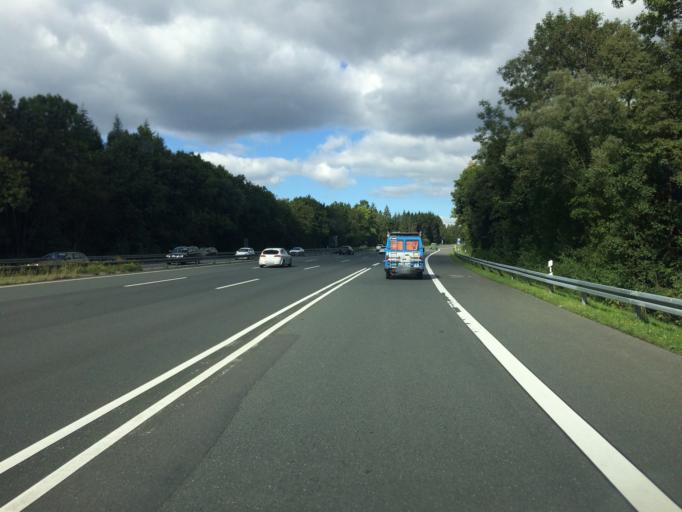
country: DE
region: Hesse
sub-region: Regierungsbezirk Giessen
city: Haiger
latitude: 50.7653
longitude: 8.1518
